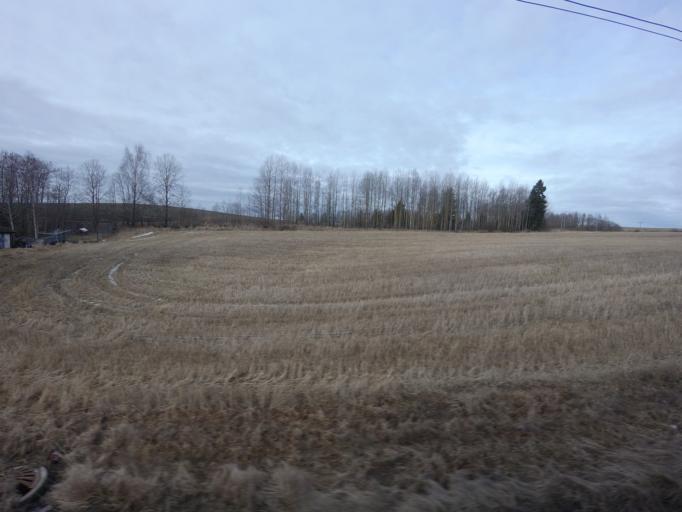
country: NO
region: Akershus
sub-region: Enebakk
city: Flateby
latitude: 59.8686
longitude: 11.2226
